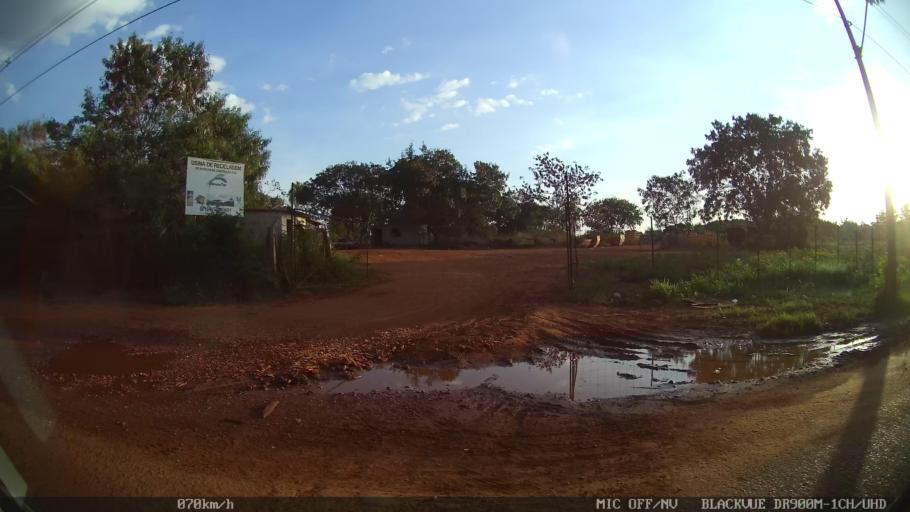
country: BR
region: Sao Paulo
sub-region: Ribeirao Preto
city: Ribeirao Preto
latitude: -21.1128
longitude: -47.8079
